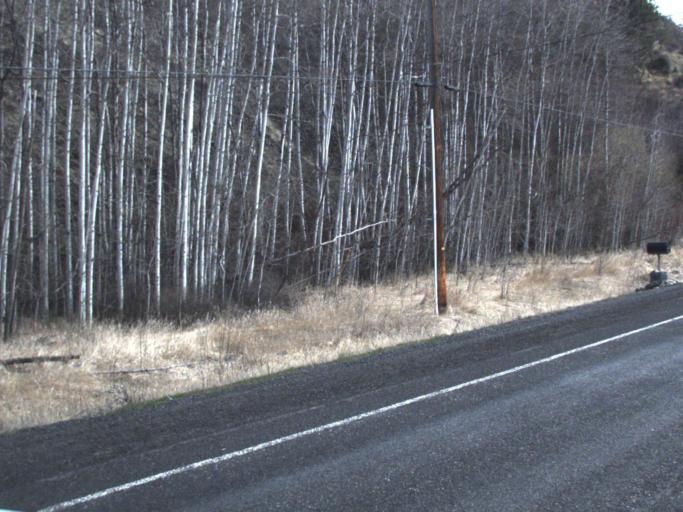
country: US
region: Washington
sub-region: Yakima County
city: Tieton
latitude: 46.8287
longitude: -120.9356
